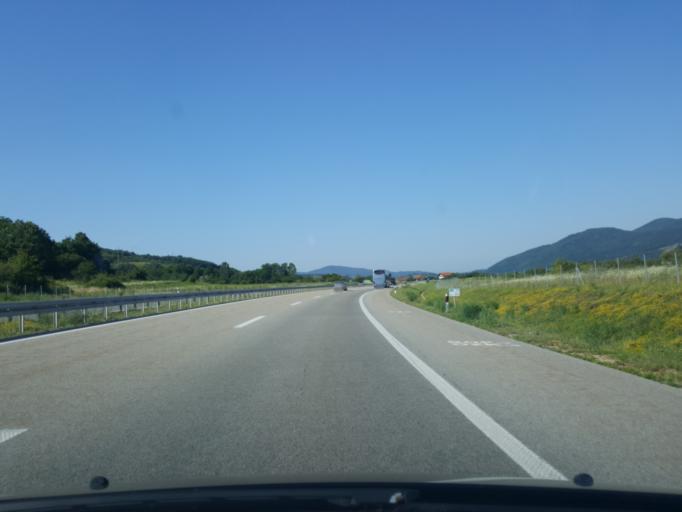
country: RS
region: Central Serbia
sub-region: Pcinjski Okrug
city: Vladicin Han
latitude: 42.6329
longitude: 22.0541
